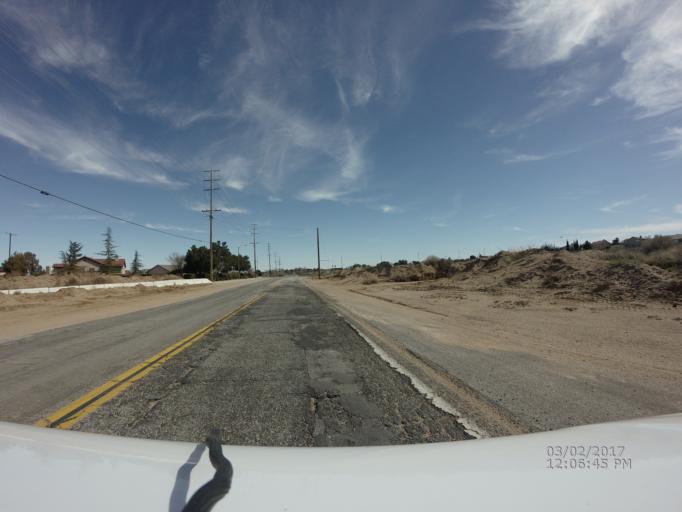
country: US
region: California
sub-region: Los Angeles County
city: Quartz Hill
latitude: 34.6456
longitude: -118.2398
